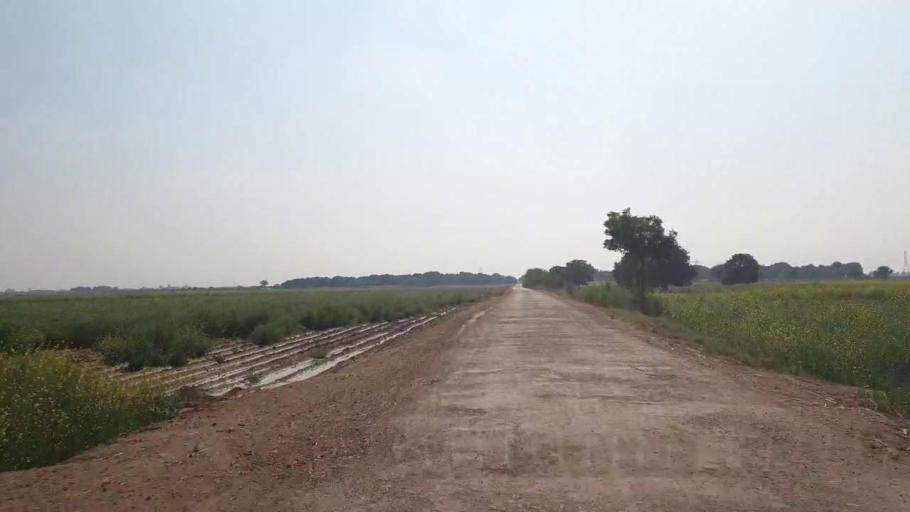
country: PK
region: Sindh
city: Chambar
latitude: 25.3938
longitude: 68.8959
